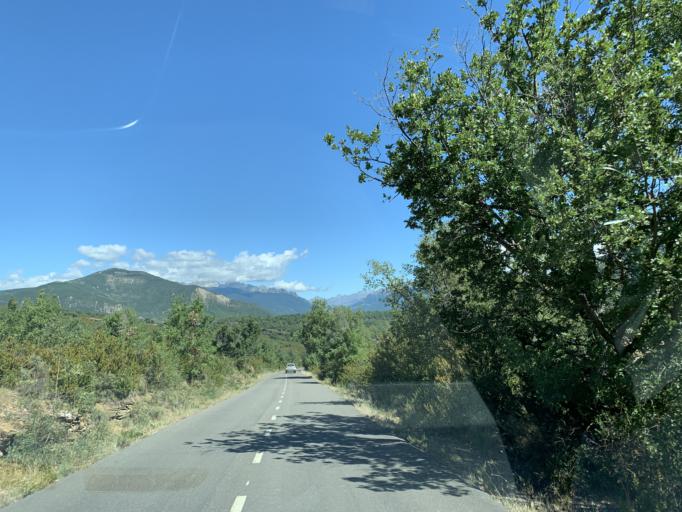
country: ES
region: Aragon
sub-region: Provincia de Huesca
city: Sabinanigo
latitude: 42.5253
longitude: -0.3240
